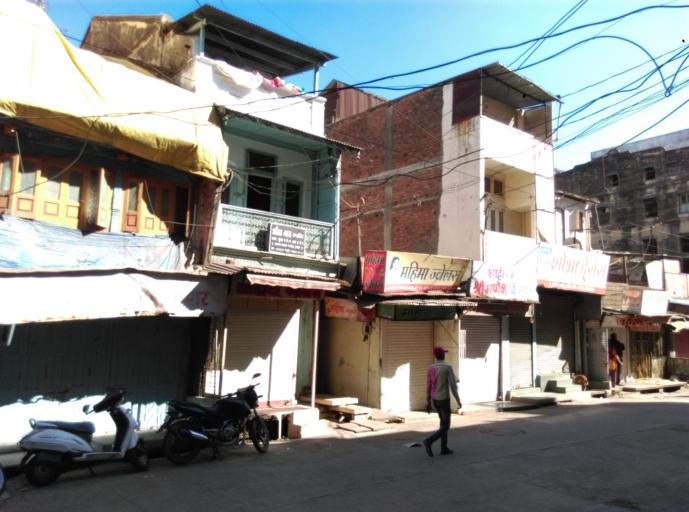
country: IN
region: Madhya Pradesh
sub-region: Indore
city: Indore
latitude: 22.7188
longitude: 75.8509
